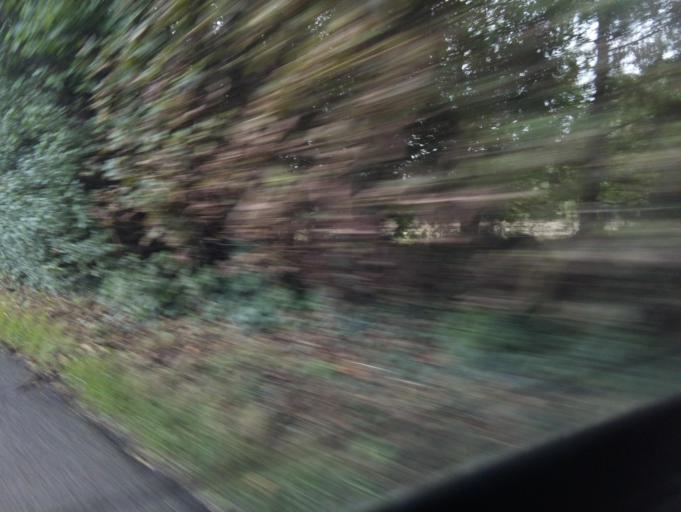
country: GB
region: England
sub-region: Staffordshire
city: Barlaston
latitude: 52.9211
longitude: -2.2187
